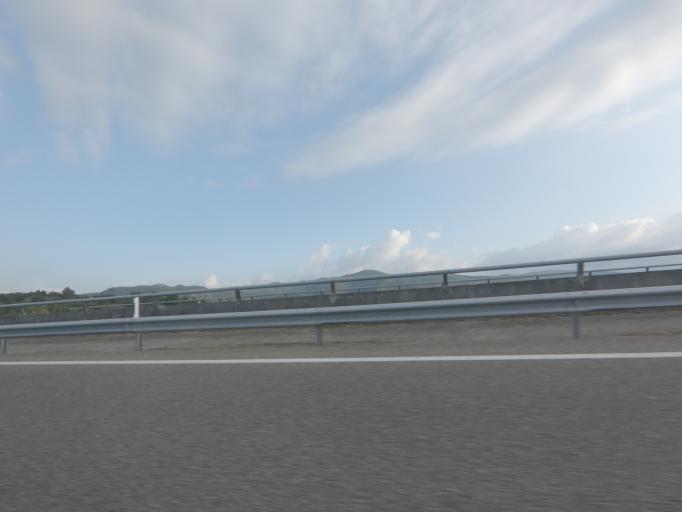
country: ES
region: Galicia
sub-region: Provincia de Ourense
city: Allariz
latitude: 42.2035
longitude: -7.7990
